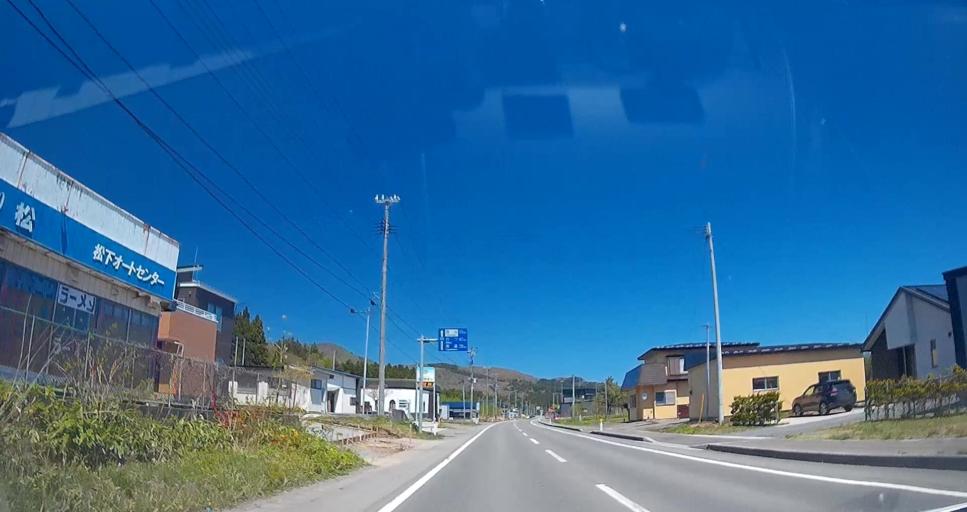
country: JP
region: Aomori
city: Mutsu
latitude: 41.0804
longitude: 141.3857
